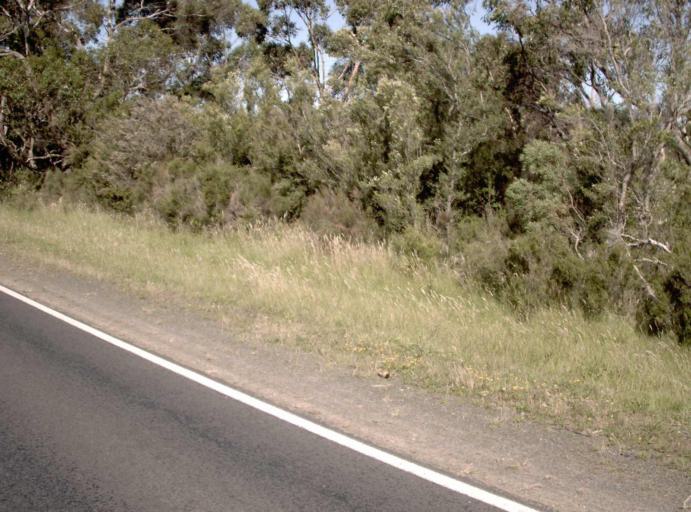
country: AU
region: Victoria
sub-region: Latrobe
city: Morwell
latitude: -38.6394
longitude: 146.5200
